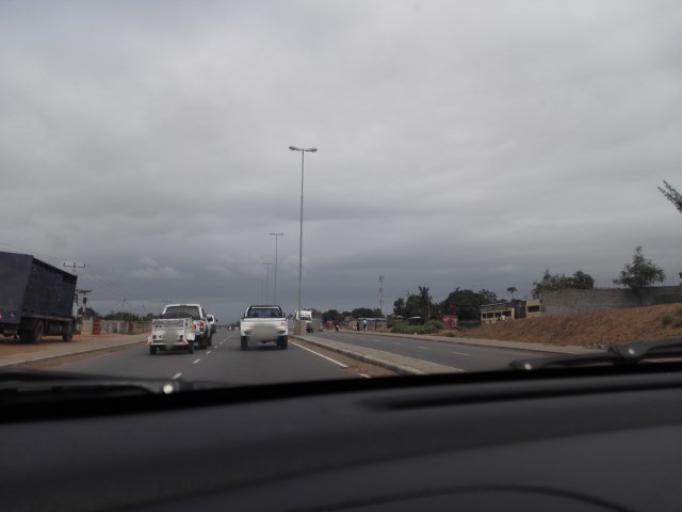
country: MZ
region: Maputo City
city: Maputo
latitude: -25.8235
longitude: 32.5919
